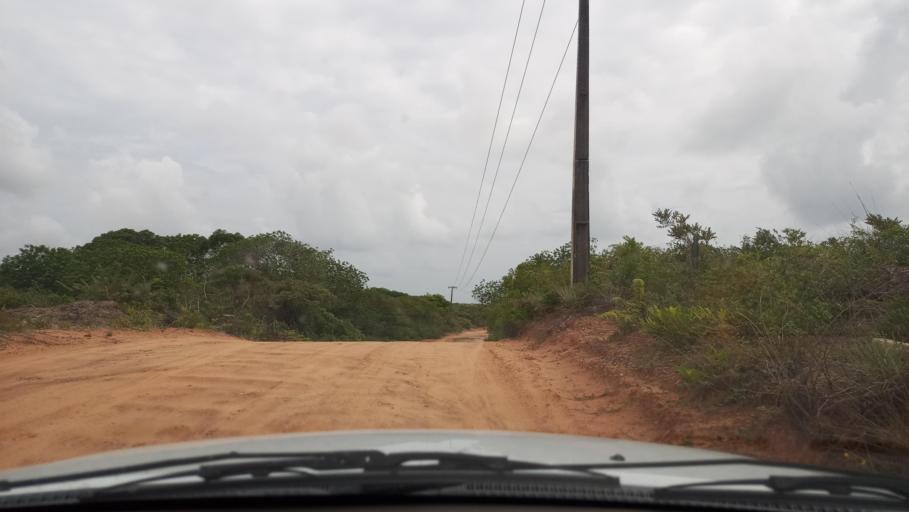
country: BR
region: Rio Grande do Norte
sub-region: Maxaranguape
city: Sao Miguel
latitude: -5.4733
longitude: -35.3013
